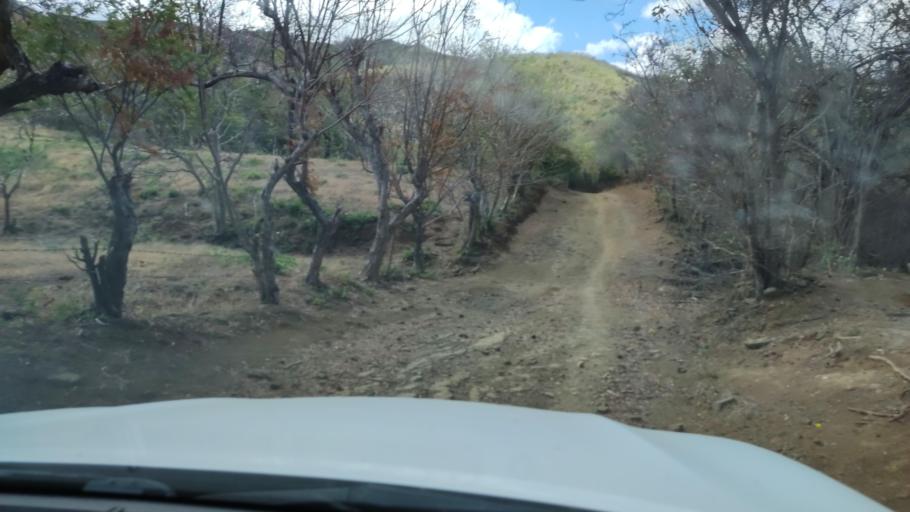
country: NI
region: Carazo
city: Santa Teresa
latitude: 11.6455
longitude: -86.2143
